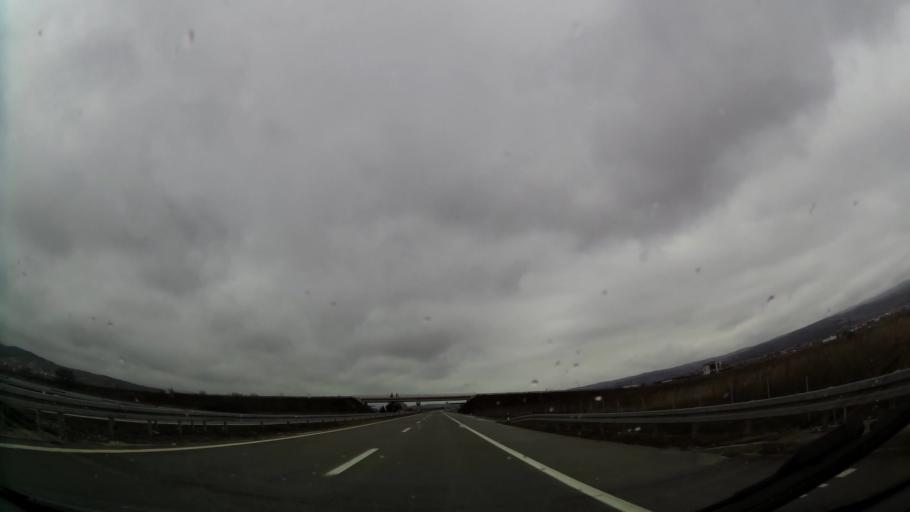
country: RS
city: Biljaca
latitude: 42.3467
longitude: 21.7222
